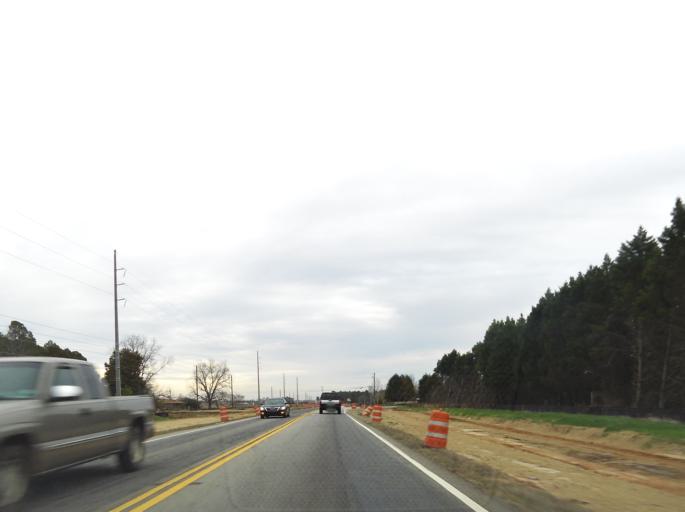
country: US
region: Georgia
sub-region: Houston County
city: Centerville
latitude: 32.5466
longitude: -83.7075
